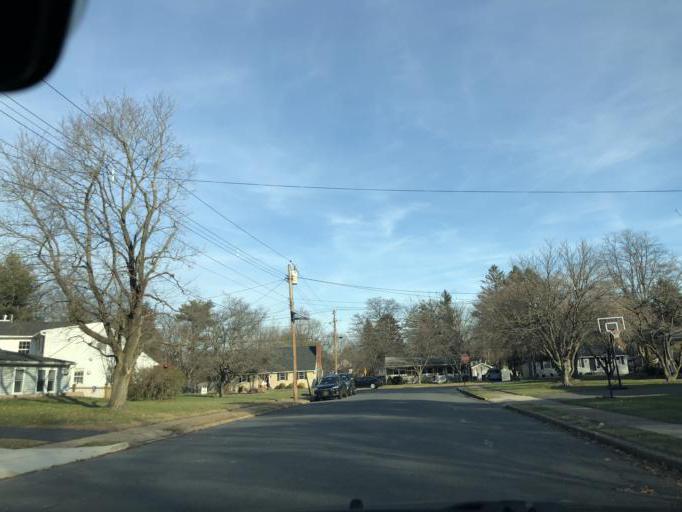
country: US
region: New Jersey
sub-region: Burlington County
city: Moorestown-Lenola
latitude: 39.9628
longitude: -74.9651
